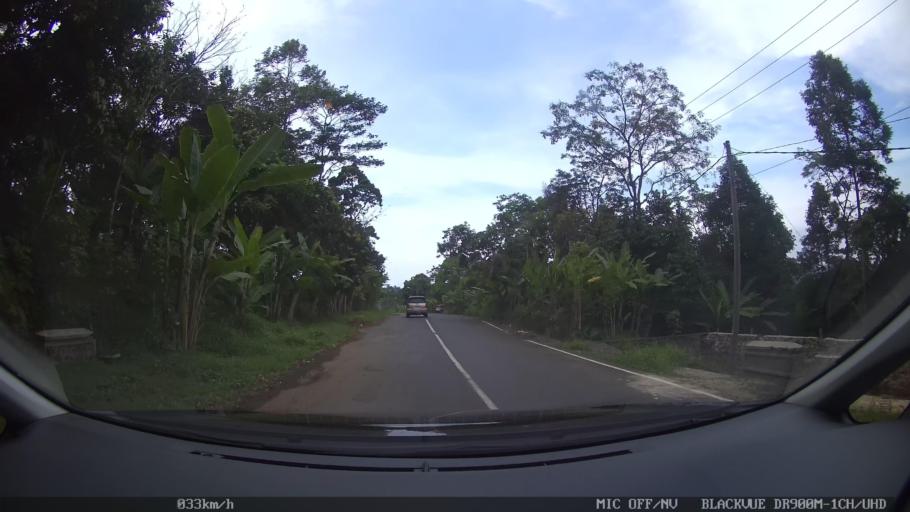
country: ID
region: Lampung
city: Bandarlampung
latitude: -5.4322
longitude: 105.2116
